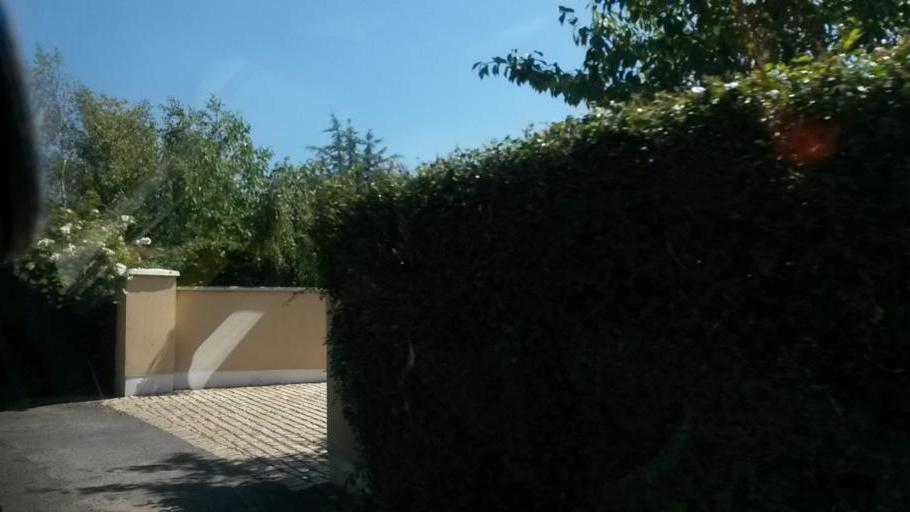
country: IE
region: Leinster
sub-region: Fingal County
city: Swords
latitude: 53.5205
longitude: -6.2788
